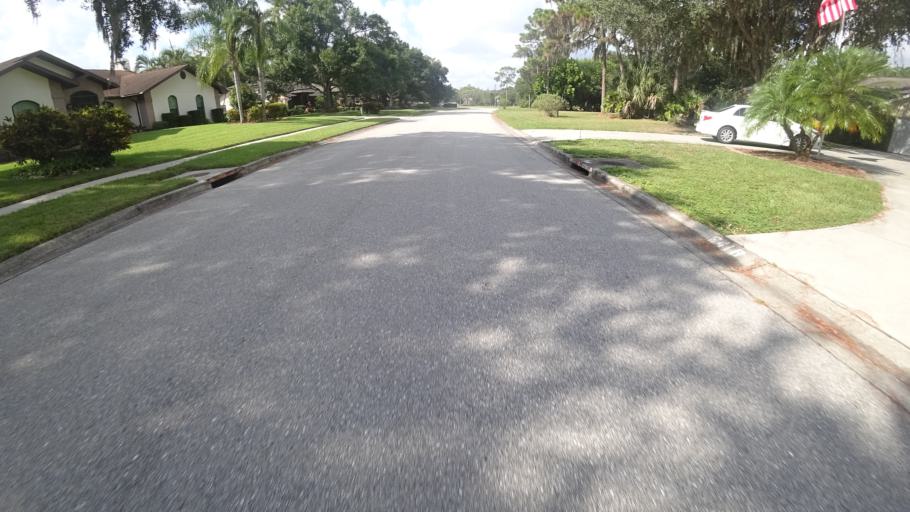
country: US
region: Florida
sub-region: Sarasota County
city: The Meadows
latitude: 27.4248
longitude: -82.4427
